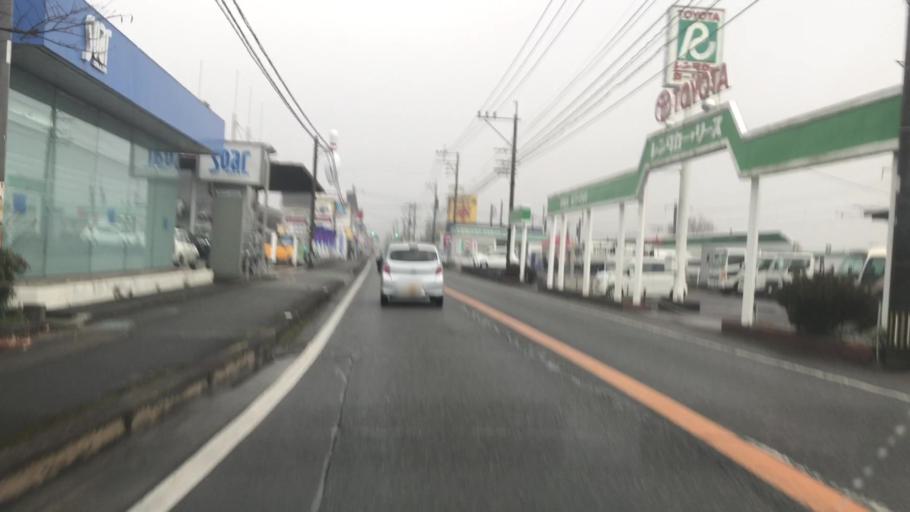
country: JP
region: Saga Prefecture
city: Takeocho-takeo
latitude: 33.2059
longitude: 130.0379
